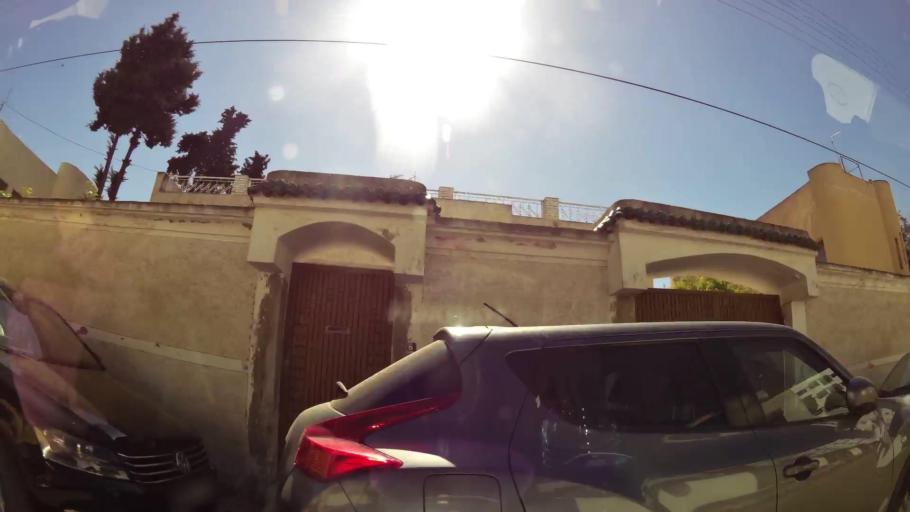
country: MA
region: Fes-Boulemane
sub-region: Fes
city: Fes
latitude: 34.0254
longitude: -4.9926
